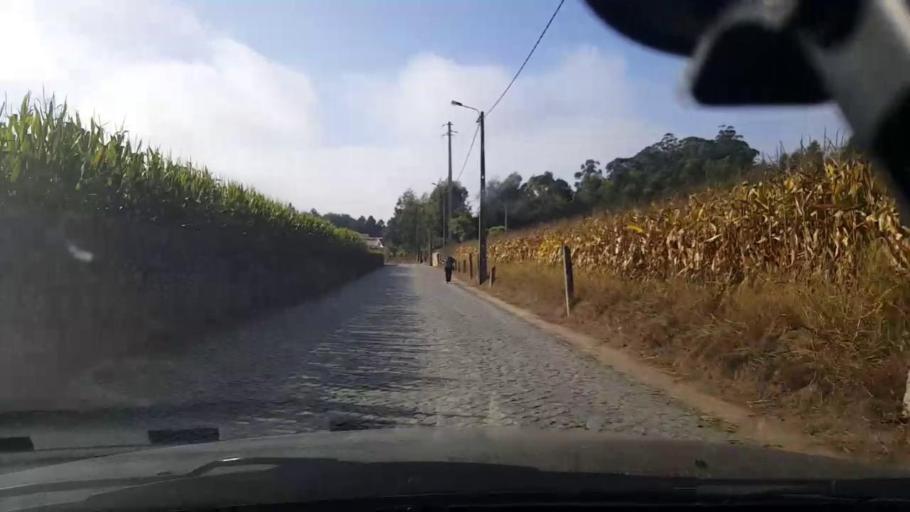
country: PT
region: Porto
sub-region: Maia
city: Gemunde
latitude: 41.2686
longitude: -8.6758
